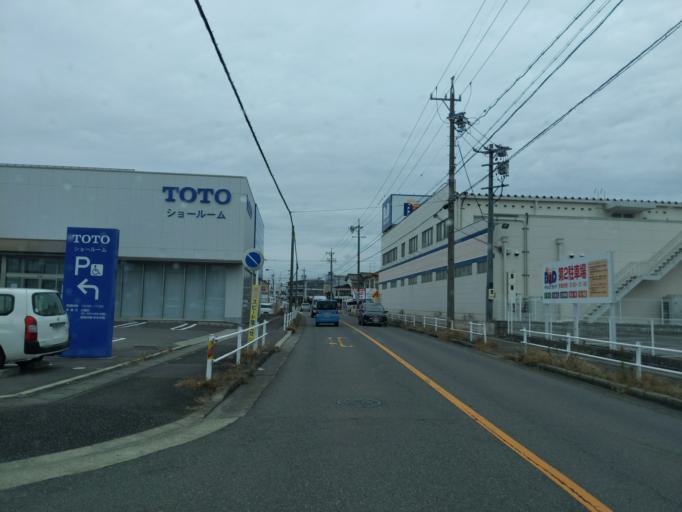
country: JP
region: Aichi
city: Kasugai
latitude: 35.2652
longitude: 136.9855
